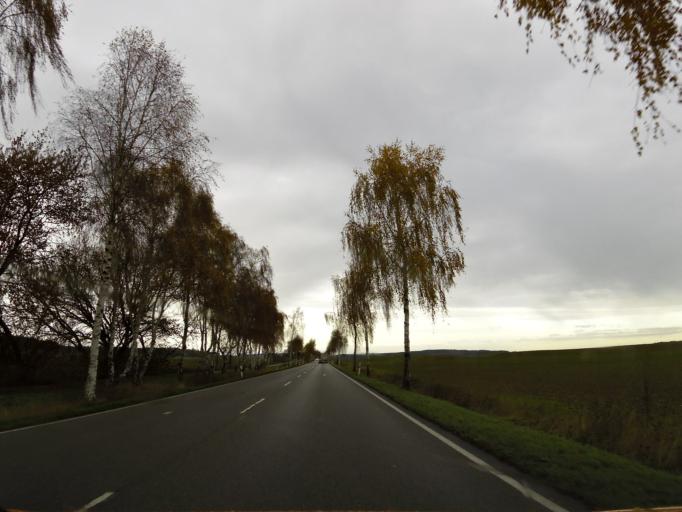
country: DE
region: Saxony-Anhalt
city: Gardelegen
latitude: 52.5812
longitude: 11.3534
